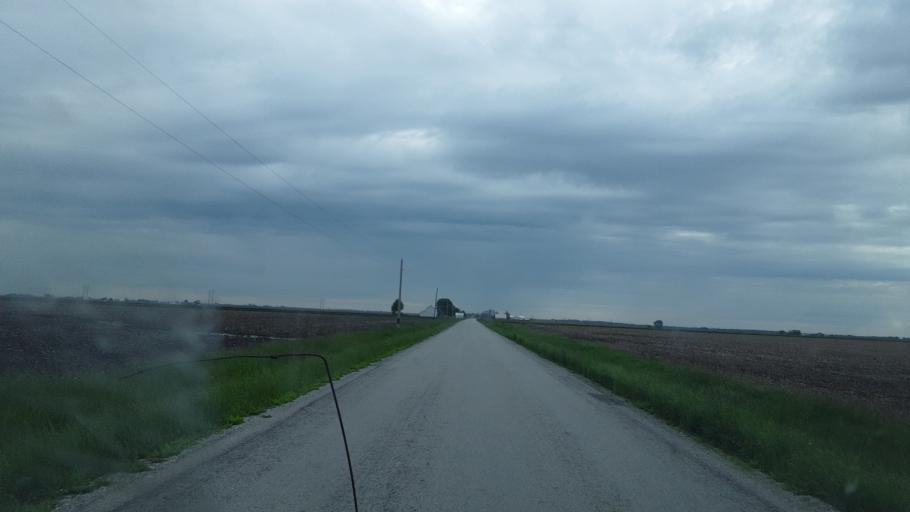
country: US
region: Illinois
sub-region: McDonough County
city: Macomb
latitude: 40.3816
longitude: -90.5400
